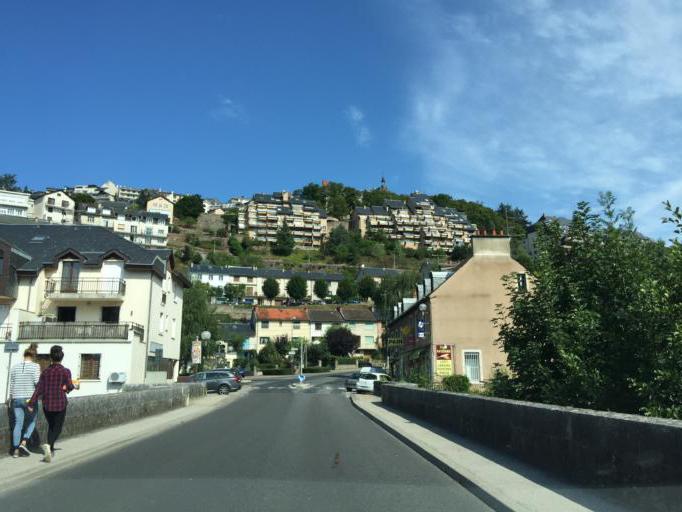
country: FR
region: Midi-Pyrenees
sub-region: Departement de l'Aveyron
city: Le Monastere
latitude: 44.3449
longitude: 2.5803
